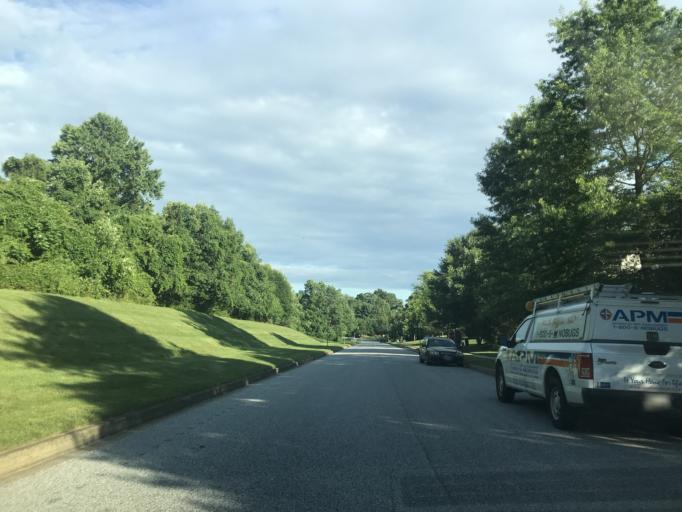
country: US
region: Maryland
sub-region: Harford County
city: South Bel Air
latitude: 39.5635
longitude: -76.3268
